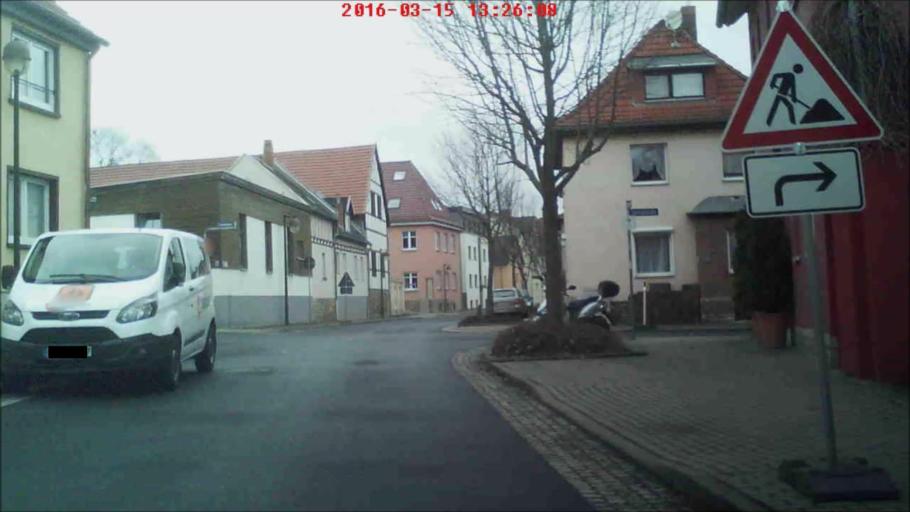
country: DE
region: Thuringia
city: Ingersleben
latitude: 50.9357
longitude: 10.9913
